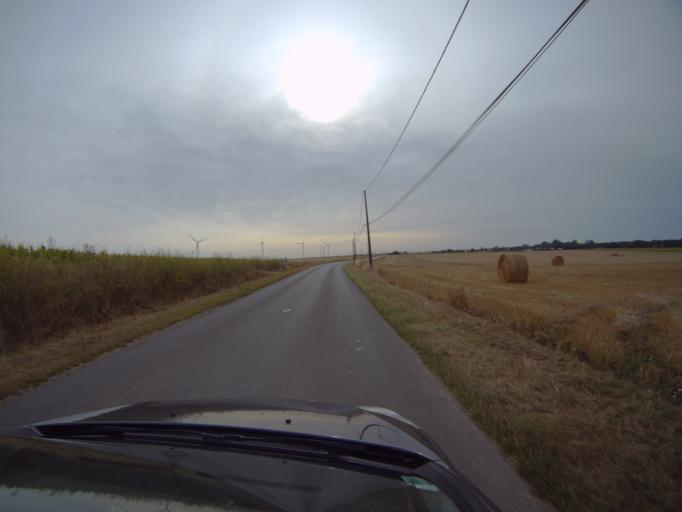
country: FR
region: Pays de la Loire
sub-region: Departement de la Vendee
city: Longeville-sur-Mer
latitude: 46.4186
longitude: -1.4643
